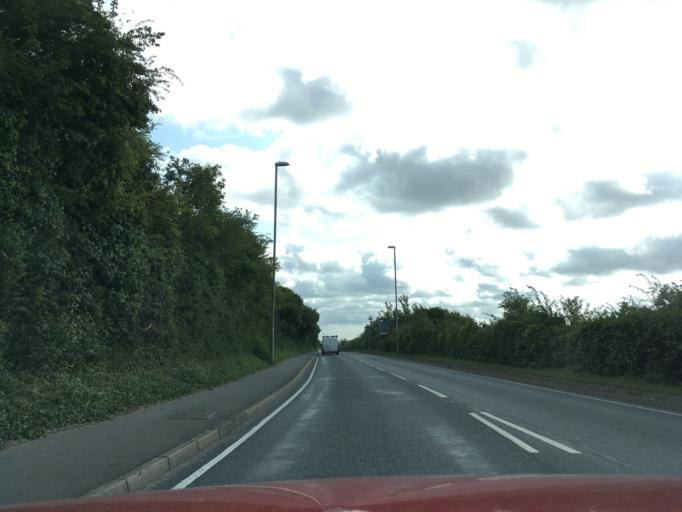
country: GB
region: England
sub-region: Hampshire
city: Waterlooville
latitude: 50.8521
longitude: -1.0327
